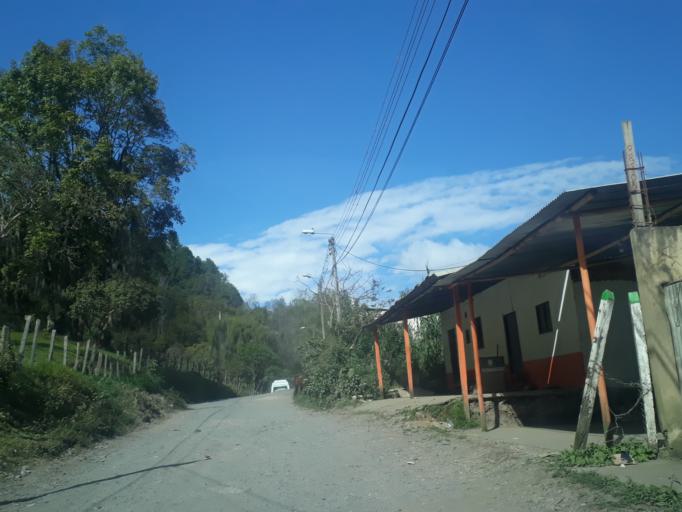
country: CO
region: Santander
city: Velez
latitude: 6.0231
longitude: -73.6690
